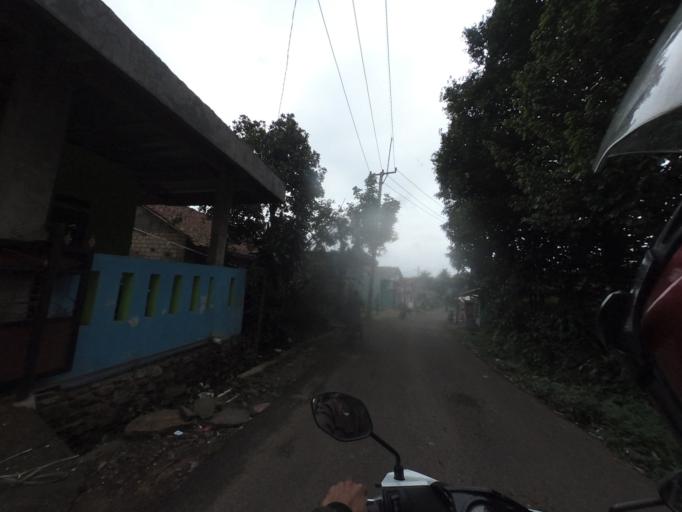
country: ID
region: West Java
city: Bogor
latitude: -6.6321
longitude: 106.7441
